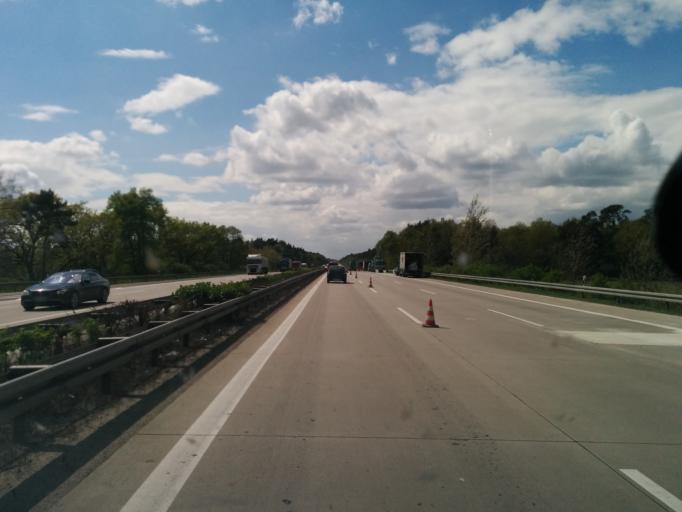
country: DE
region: Saxony-Anhalt
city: Burg bei Magdeburg
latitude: 52.2324
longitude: 11.8897
